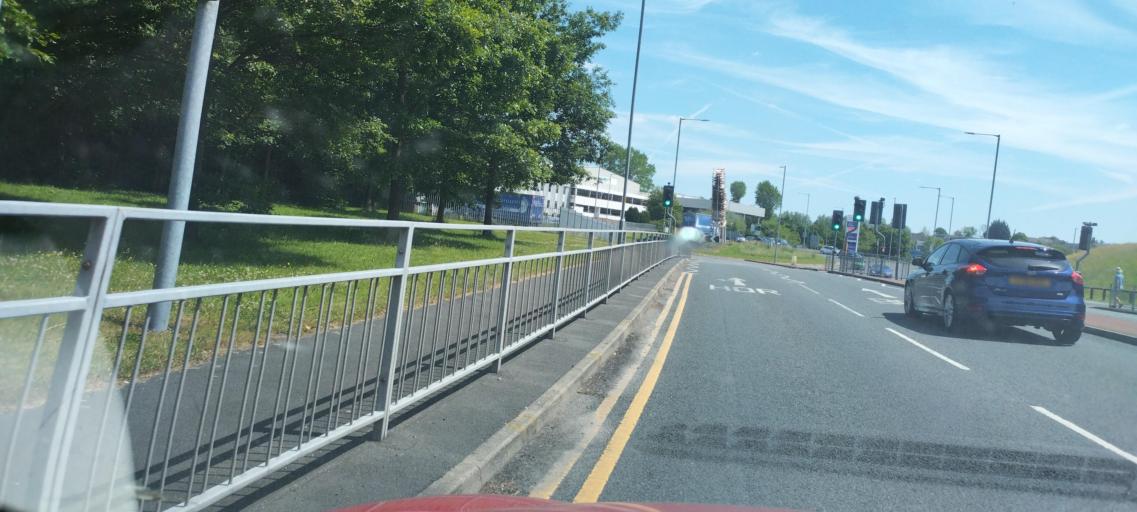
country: GB
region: England
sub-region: Borough of Bolton
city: Horwich
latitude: 53.5829
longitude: -2.5312
